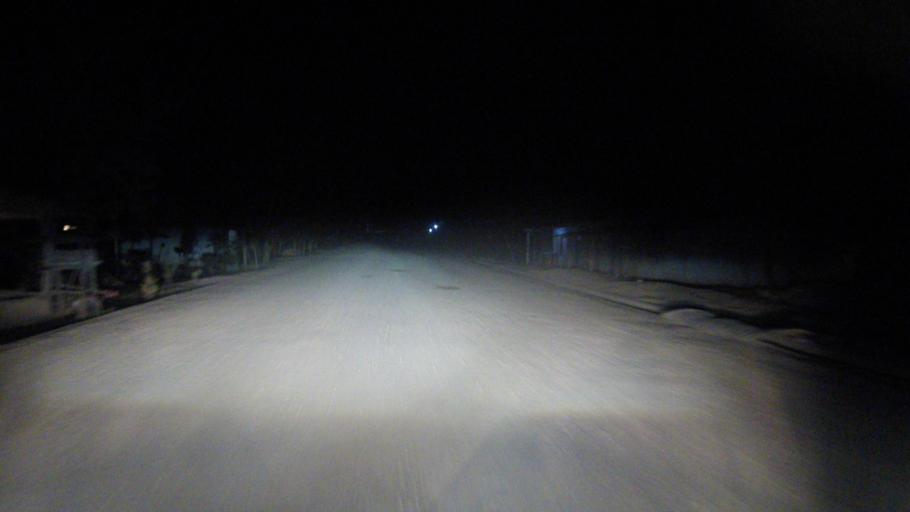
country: TL
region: Viqueque
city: Viqueque
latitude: -8.8245
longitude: 126.5299
